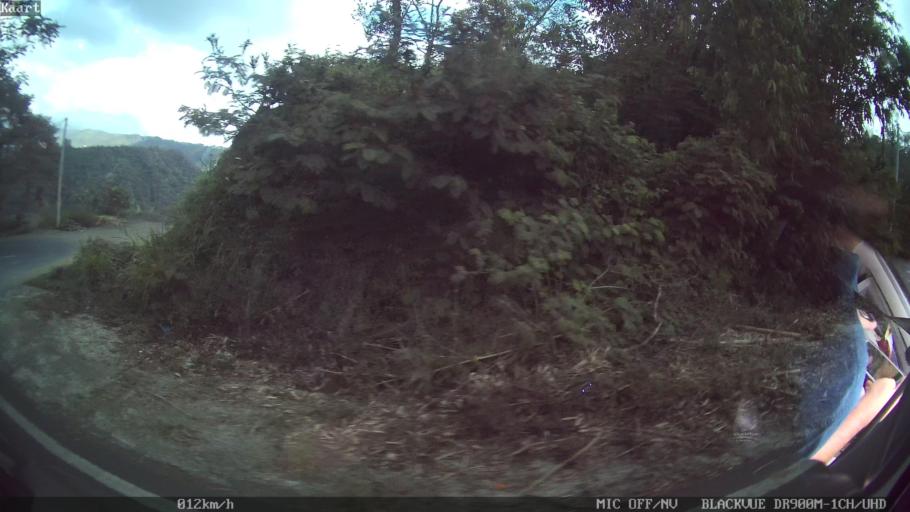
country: ID
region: Bali
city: Banjar Kedisan
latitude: -8.2592
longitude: 115.3425
